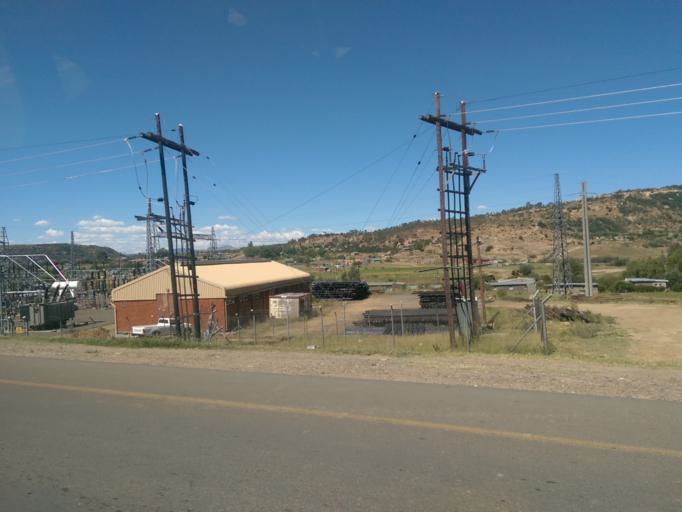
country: LS
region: Maseru
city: Maseru
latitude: -29.4067
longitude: 27.5621
